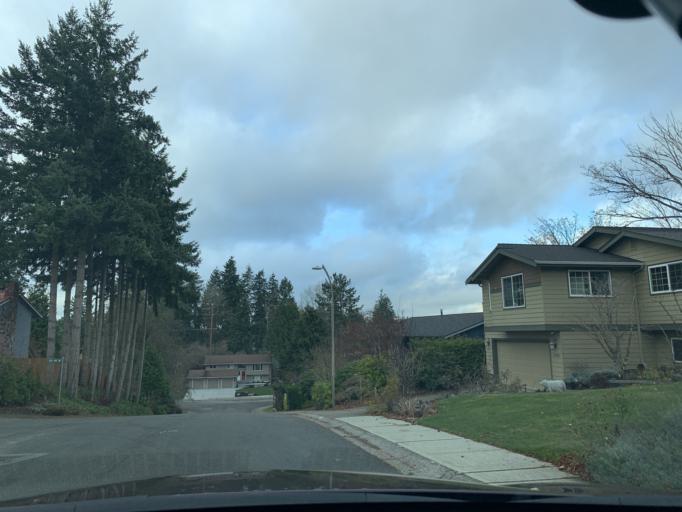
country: US
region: Washington
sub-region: King County
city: Kingsgate
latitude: 47.7360
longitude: -122.1698
